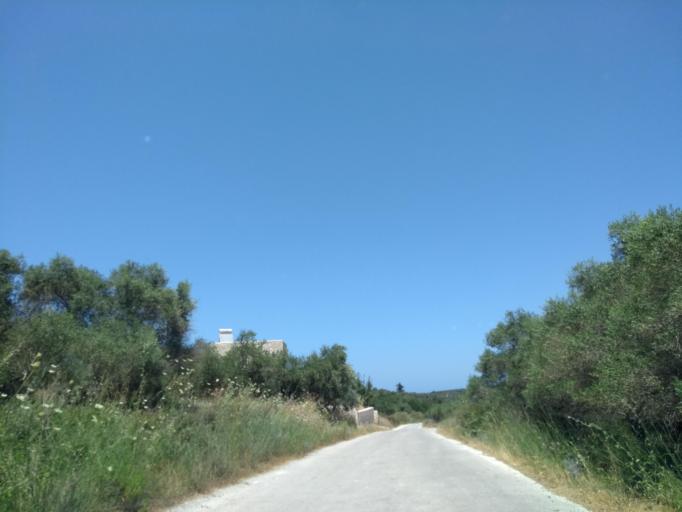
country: GR
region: Crete
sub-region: Nomos Chanias
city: Georgioupolis
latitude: 35.3250
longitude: 24.3149
